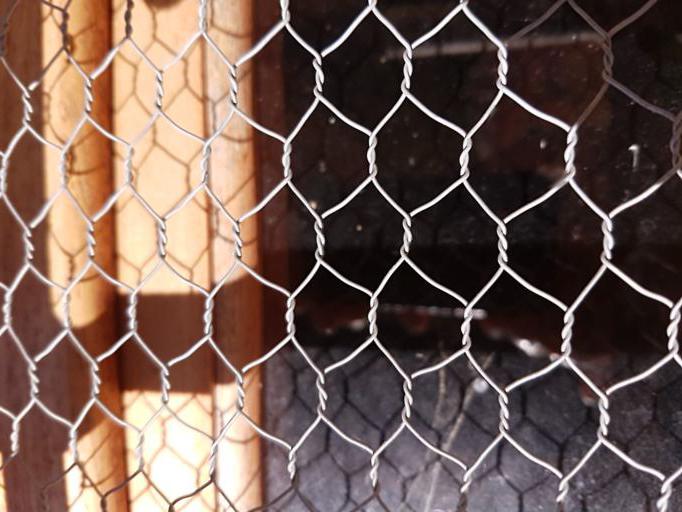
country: GR
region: Ionian Islands
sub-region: Nomos Kerkyras
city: Acharavi
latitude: 39.7453
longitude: 19.8823
